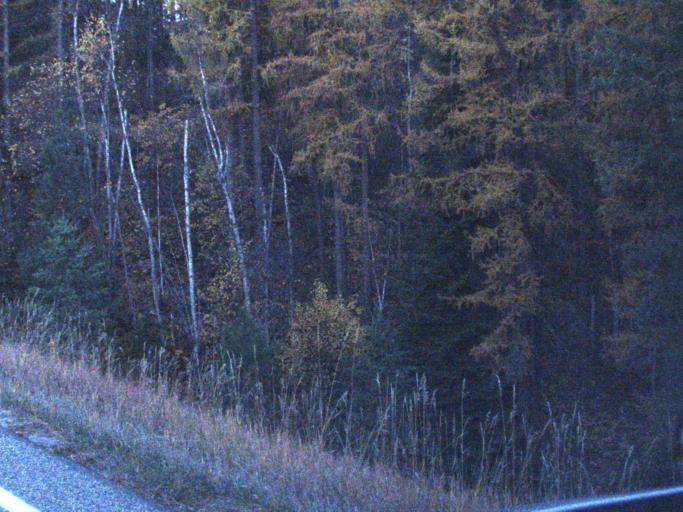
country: CA
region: British Columbia
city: Rossland
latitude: 48.9329
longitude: -117.7728
